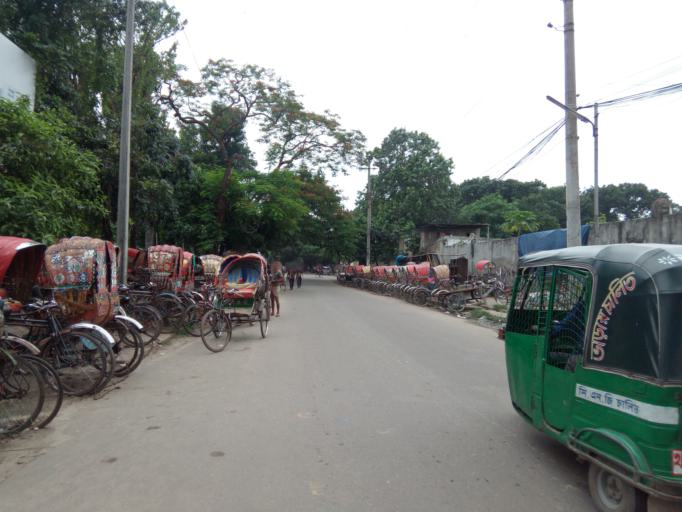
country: BD
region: Dhaka
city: Paltan
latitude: 23.7627
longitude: 90.4020
